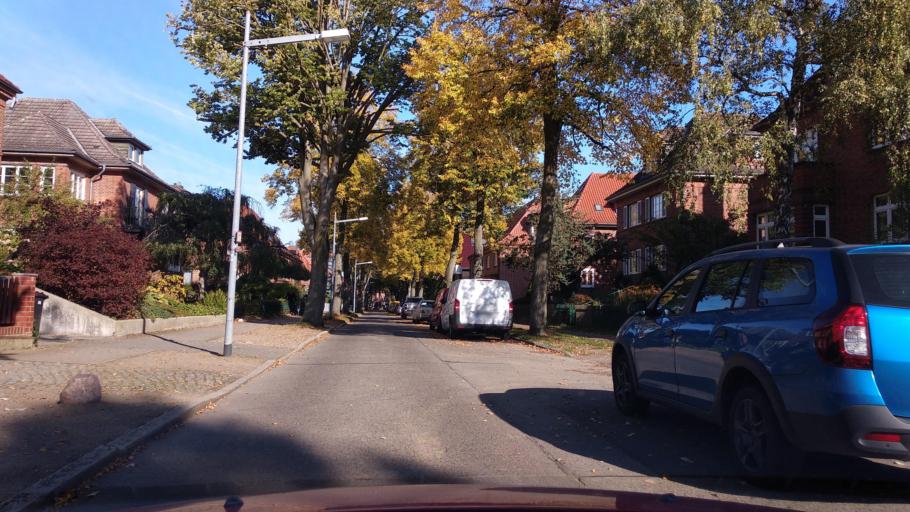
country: DE
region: Mecklenburg-Vorpommern
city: Weststadt
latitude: 53.6299
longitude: 11.3949
